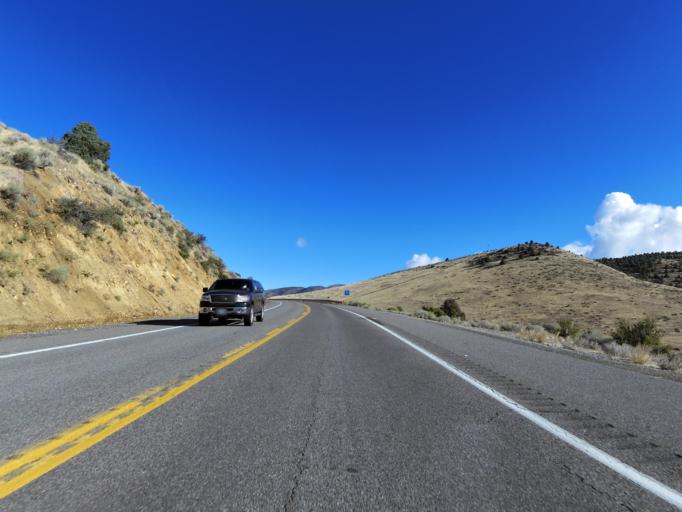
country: US
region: Nevada
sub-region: Lyon County
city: Smith Valley
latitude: 38.7052
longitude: -119.5522
